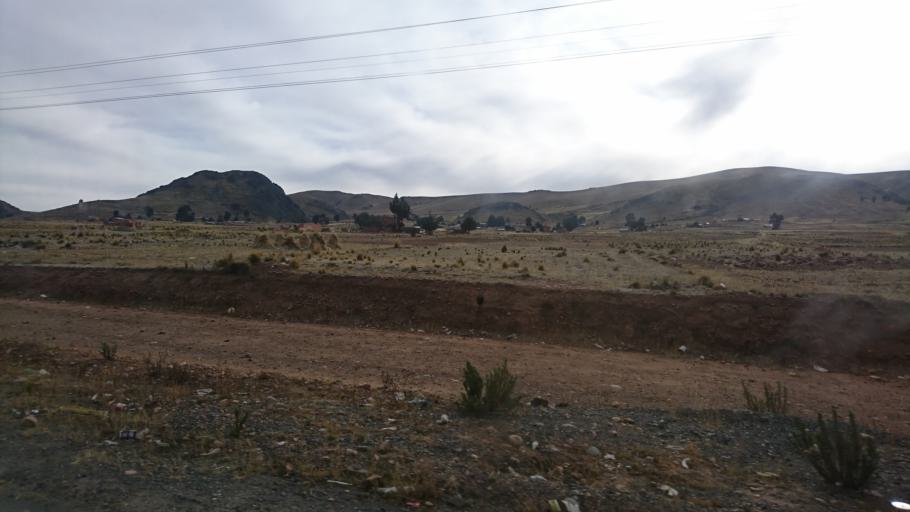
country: BO
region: La Paz
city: Batallas
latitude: -16.4071
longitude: -68.3525
